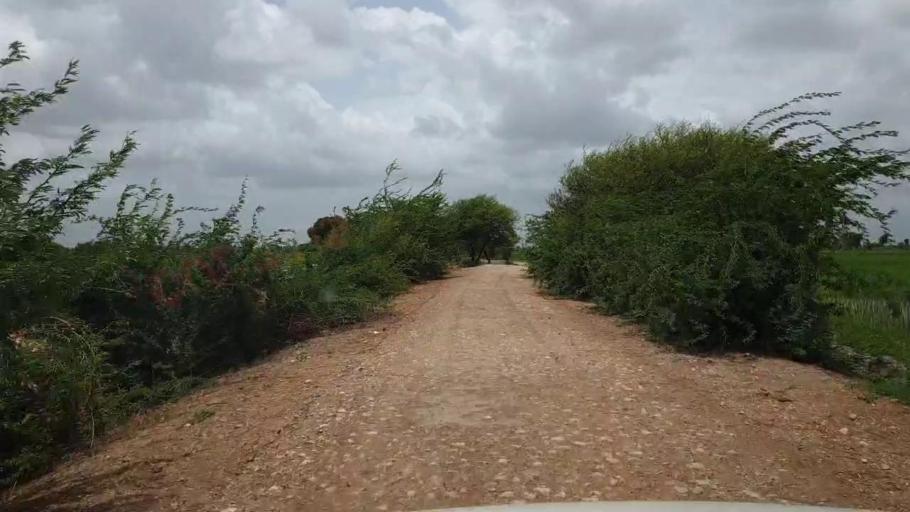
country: PK
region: Sindh
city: Kario
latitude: 24.7401
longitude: 68.5241
